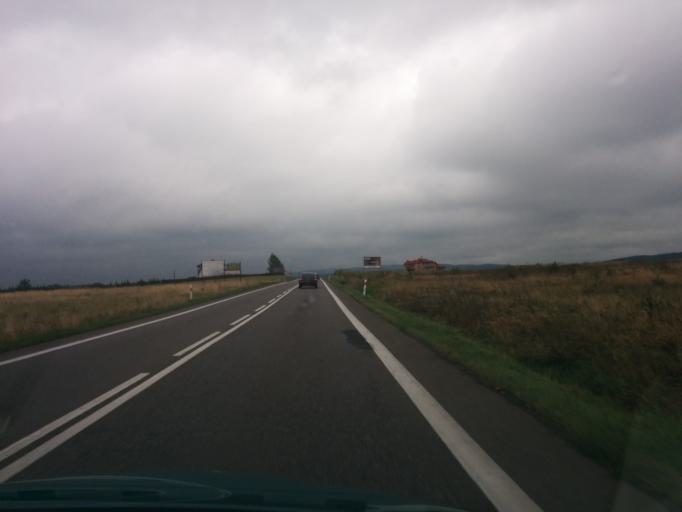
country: PL
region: Subcarpathian Voivodeship
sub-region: Powiat sanocki
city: Strachocina
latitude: 49.5820
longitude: 22.1441
